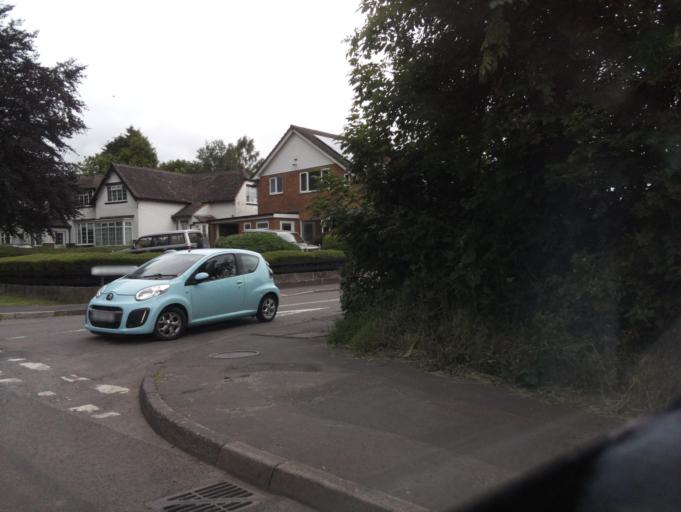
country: GB
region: England
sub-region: Derbyshire
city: Swadlincote
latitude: 52.7778
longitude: -1.5405
